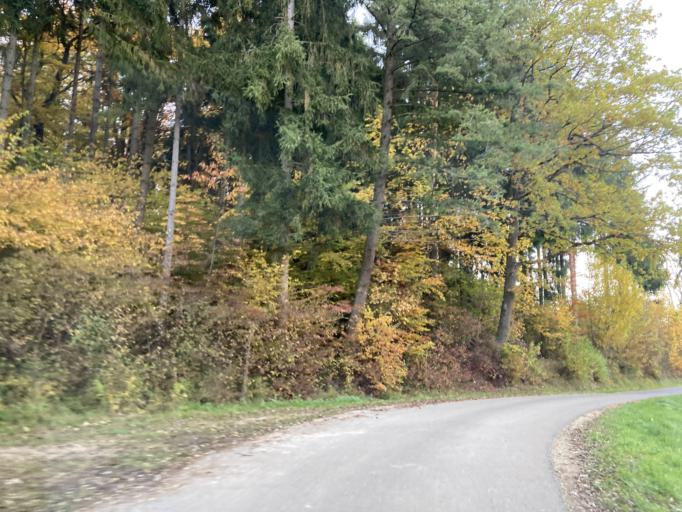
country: DE
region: Baden-Wuerttemberg
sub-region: Tuebingen Region
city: Mossingen
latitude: 48.3804
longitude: 9.0289
